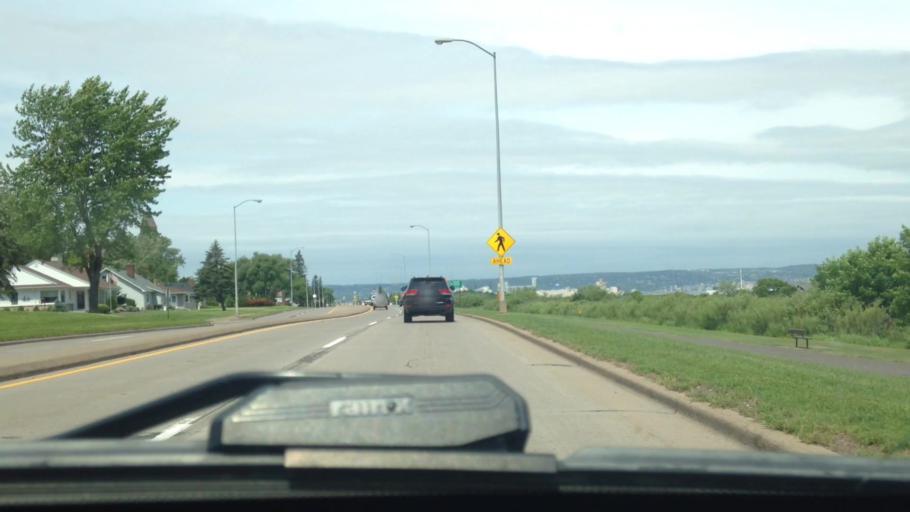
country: US
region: Wisconsin
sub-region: Douglas County
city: Superior
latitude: 46.7168
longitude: -92.0603
